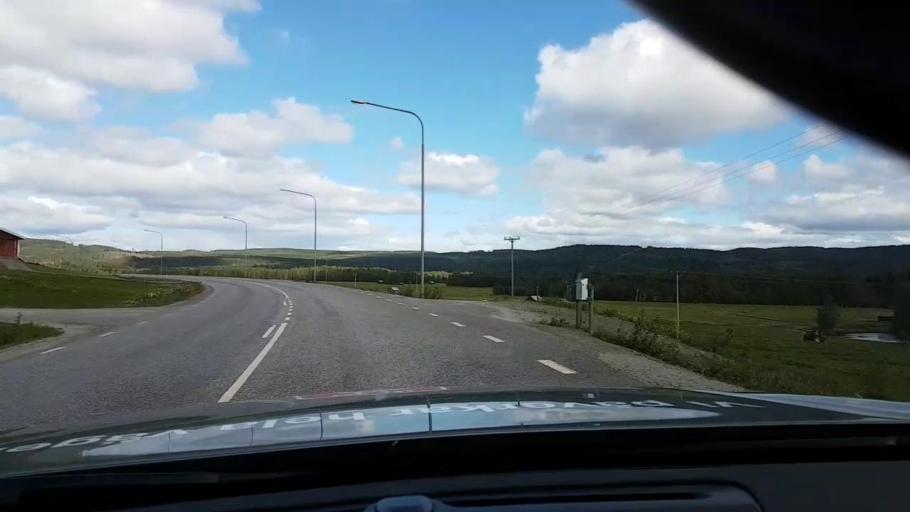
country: SE
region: Vaesternorrland
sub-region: OErnskoeldsviks Kommun
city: Bredbyn
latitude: 63.4966
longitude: 18.0826
